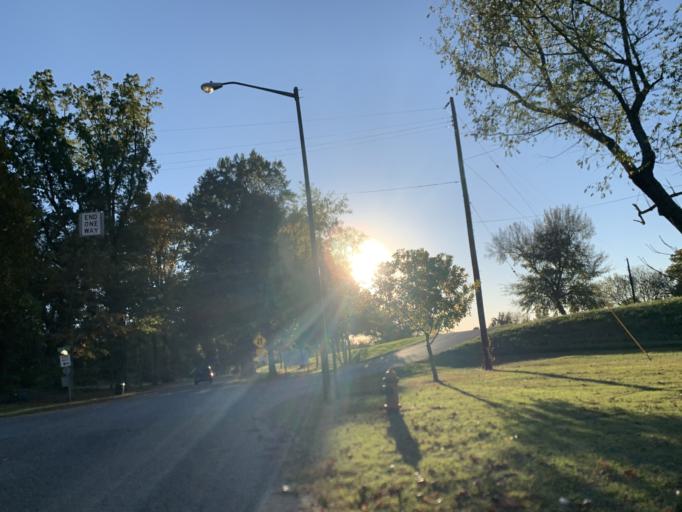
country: US
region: Indiana
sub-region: Floyd County
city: New Albany
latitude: 38.2722
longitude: -85.8178
